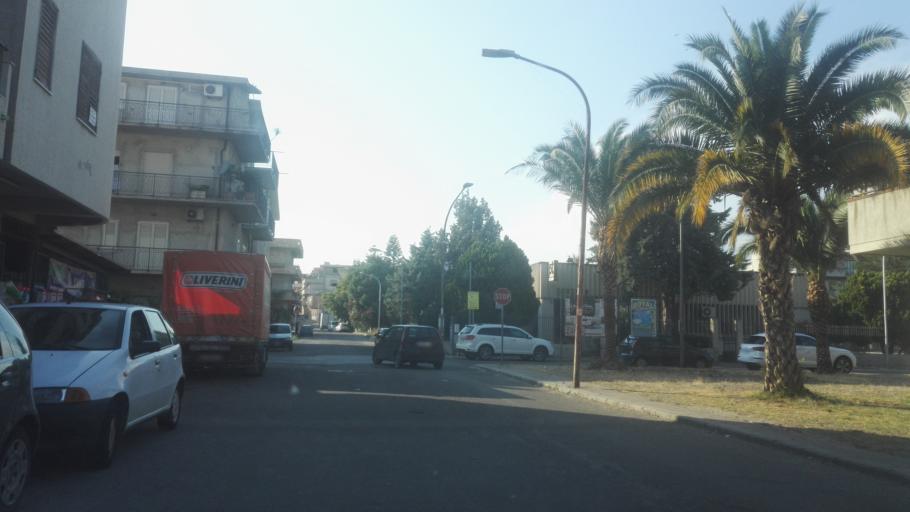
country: IT
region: Calabria
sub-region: Provincia di Reggio Calabria
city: Marina di Gioiosa Ionica
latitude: 38.3027
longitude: 16.3304
